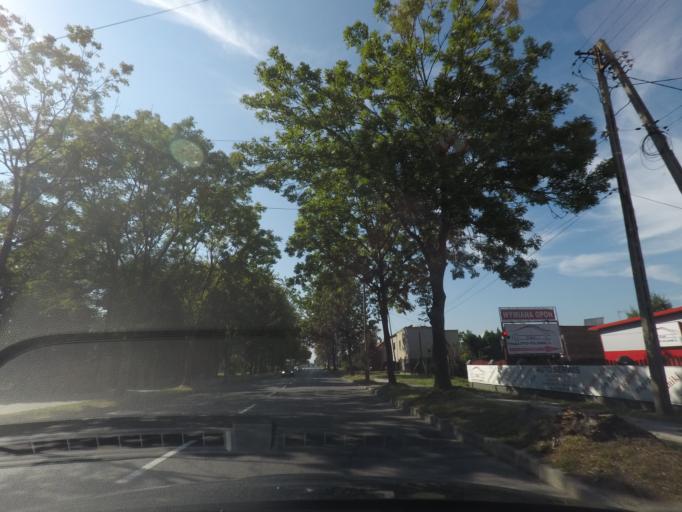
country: PL
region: Silesian Voivodeship
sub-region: Zory
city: Zory
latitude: 50.0500
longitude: 18.6889
